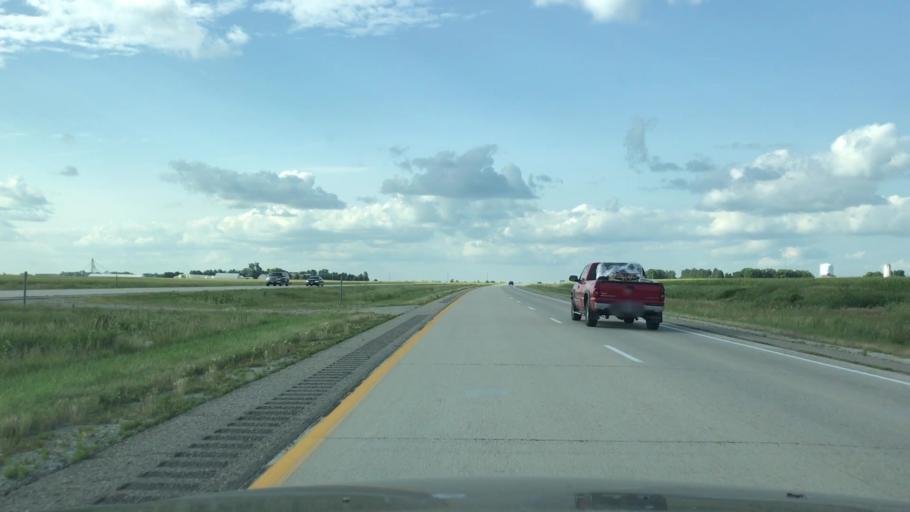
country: US
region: Iowa
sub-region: Osceola County
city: Sibley
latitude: 43.4540
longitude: -95.7133
